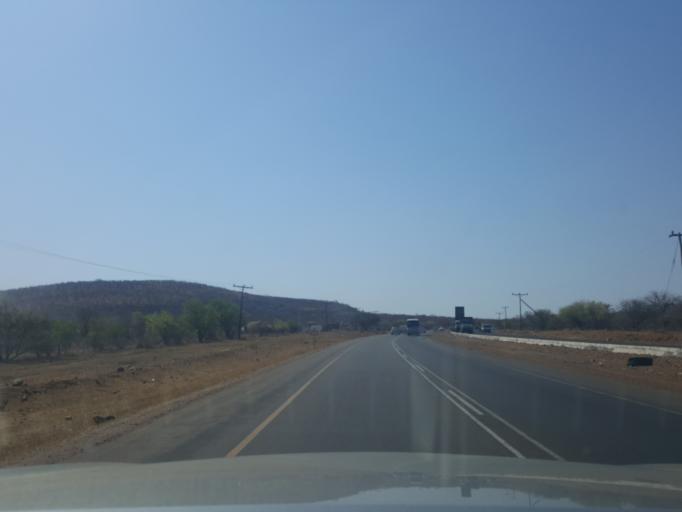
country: BW
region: Kweneng
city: Gabane
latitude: -24.7571
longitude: 25.8295
